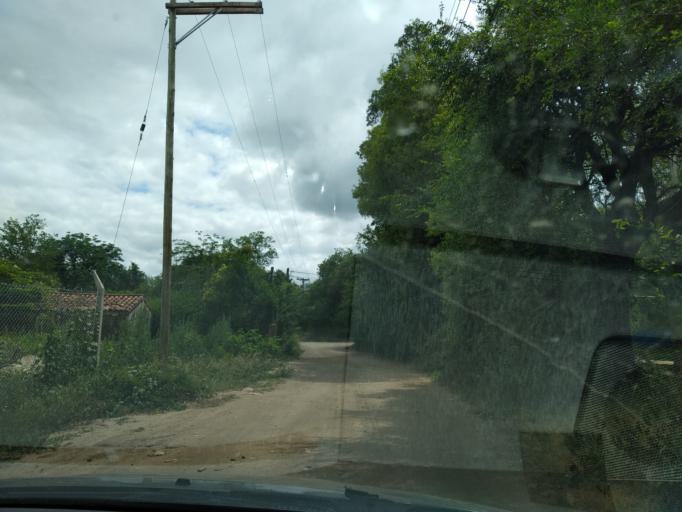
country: AR
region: Cordoba
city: Villa Las Rosas
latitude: -31.9427
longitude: -65.0308
